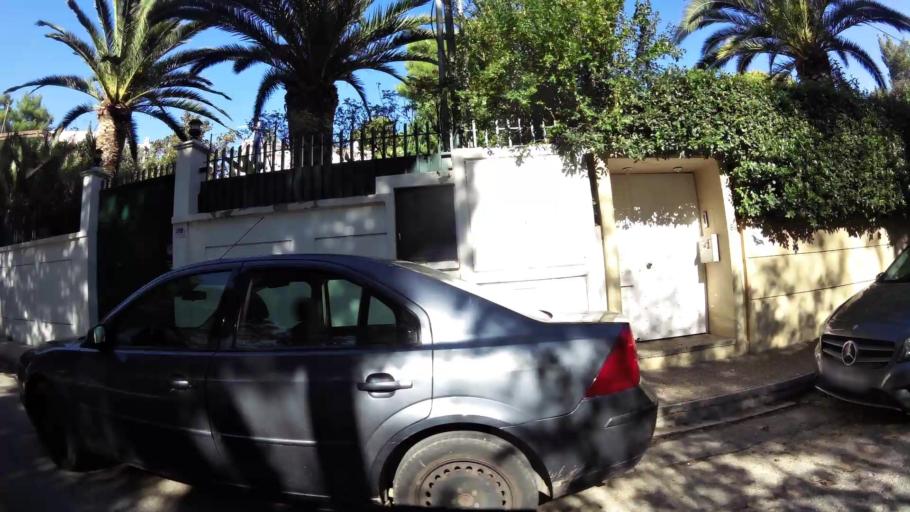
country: GR
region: Attica
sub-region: Nomarchia Athinas
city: Ekali
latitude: 38.1153
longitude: 23.8485
